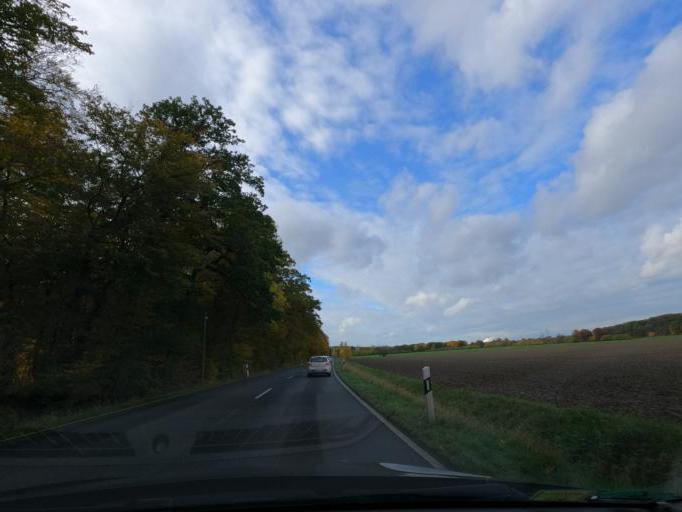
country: DE
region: Lower Saxony
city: Wolfenbuettel
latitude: 52.1369
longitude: 10.5067
